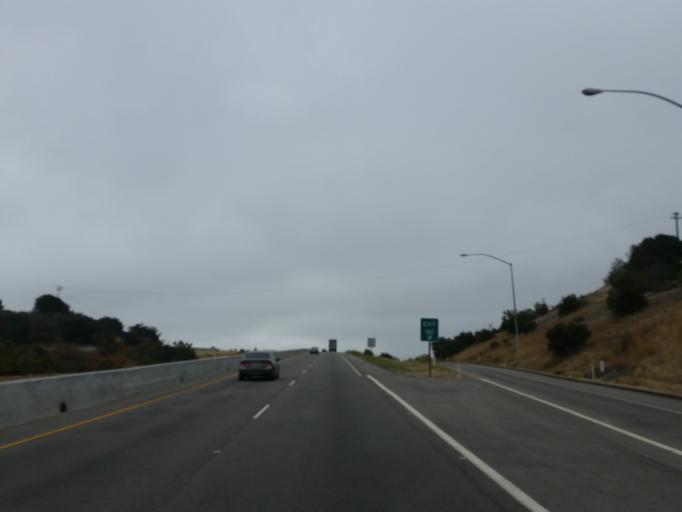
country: US
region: California
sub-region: San Luis Obispo County
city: Nipomo
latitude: 35.0752
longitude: -120.5206
